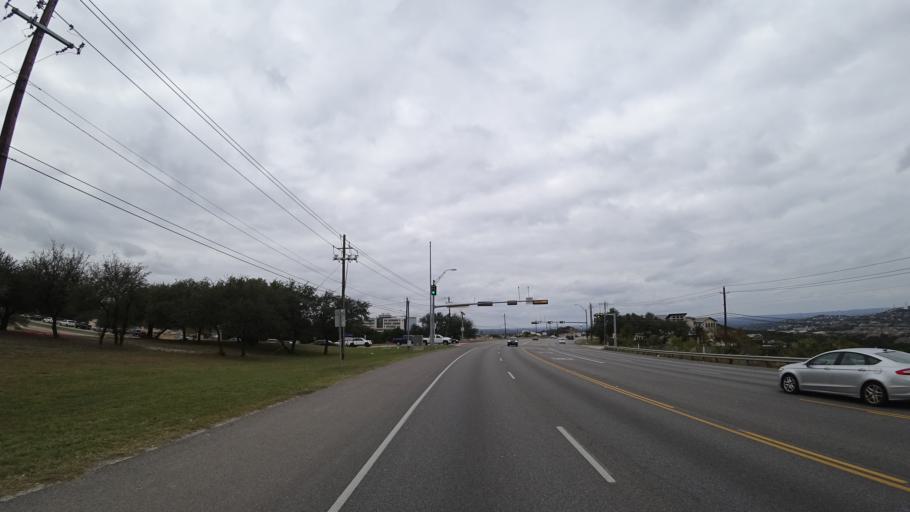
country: US
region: Texas
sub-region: Travis County
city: The Hills
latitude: 30.3300
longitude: -97.9667
